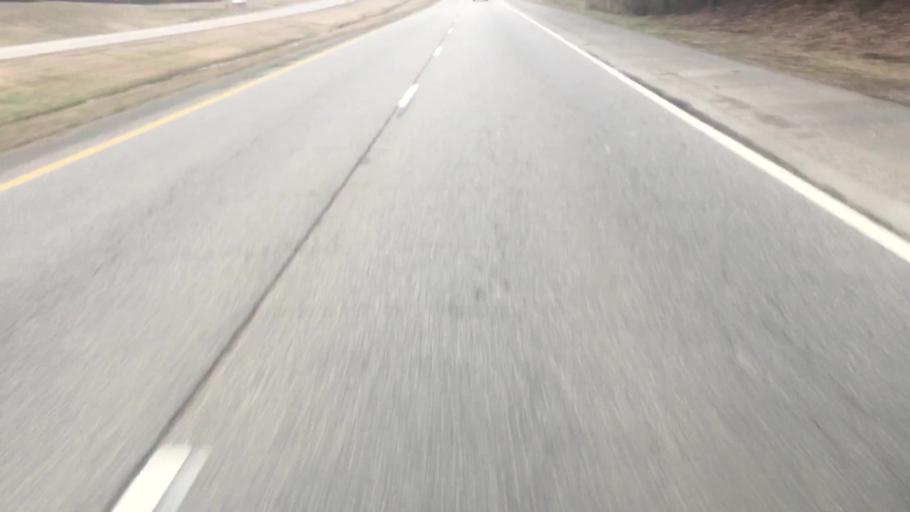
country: US
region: Alabama
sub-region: Walker County
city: Sumiton
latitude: 33.7396
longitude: -87.0318
